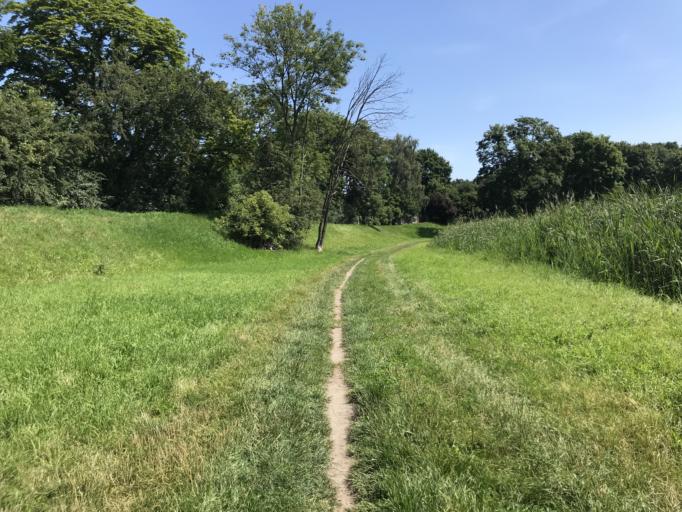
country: PL
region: Pomeranian Voivodeship
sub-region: Gdansk
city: Gdansk
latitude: 54.3393
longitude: 18.6601
